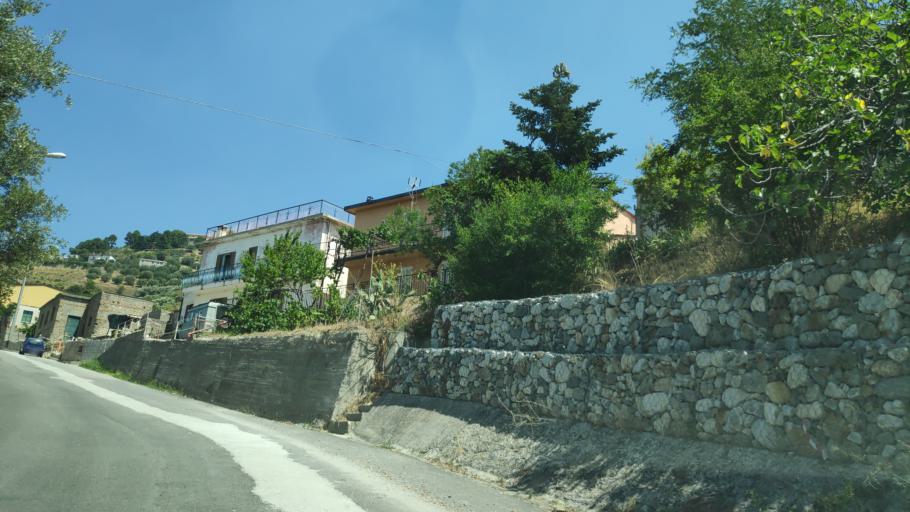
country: IT
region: Calabria
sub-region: Provincia di Reggio Calabria
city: Bova
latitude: 37.9896
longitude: 15.9287
